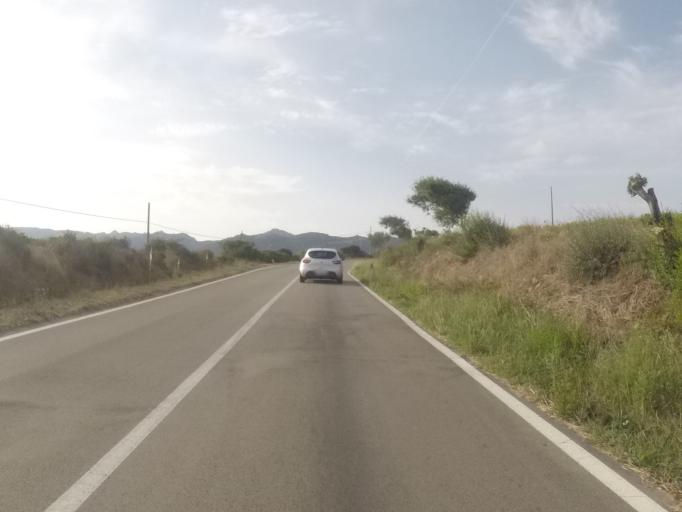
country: IT
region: Sardinia
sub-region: Provincia di Olbia-Tempio
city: Aglientu
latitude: 41.0895
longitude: 9.0271
